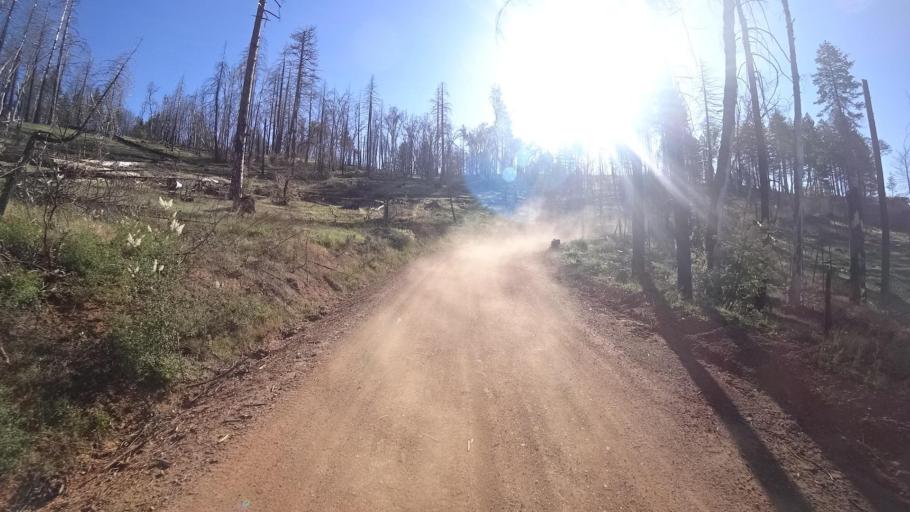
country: US
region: California
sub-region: Lake County
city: Upper Lake
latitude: 39.3598
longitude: -122.9915
